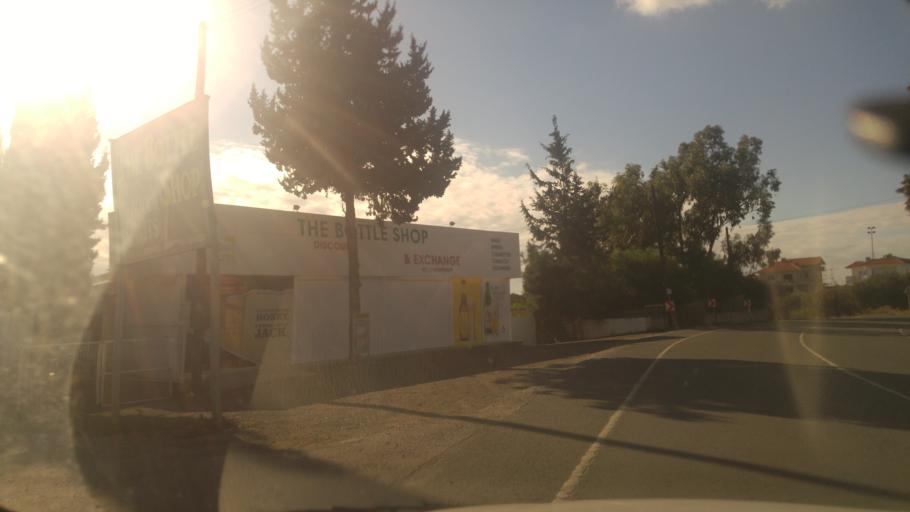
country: CY
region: Larnaka
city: Kolossi
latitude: 34.6760
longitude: 32.9432
